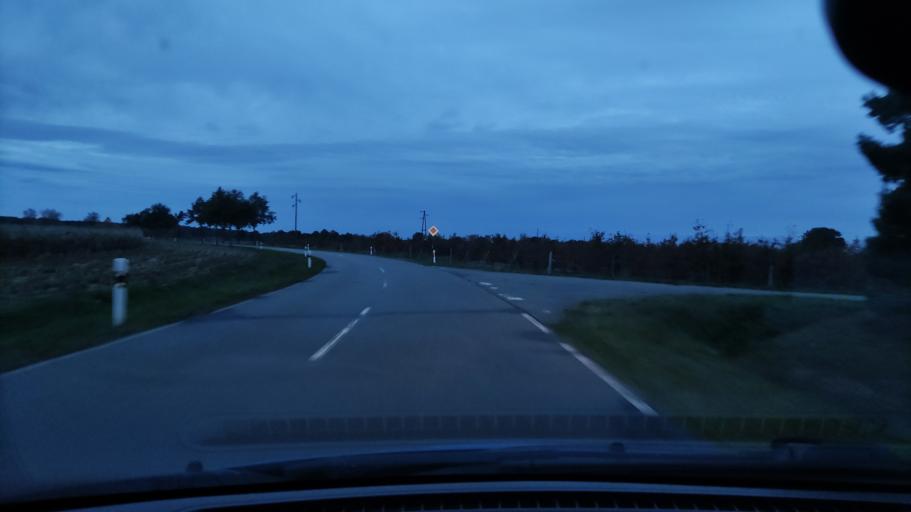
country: DE
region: Lower Saxony
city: Trebel
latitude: 52.9619
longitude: 11.3490
